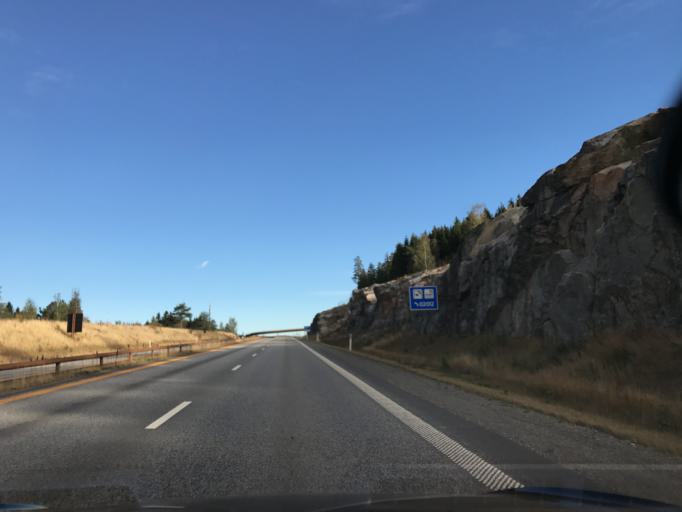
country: NO
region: Hedmark
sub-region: Stange
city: Stange
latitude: 60.5569
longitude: 11.2521
